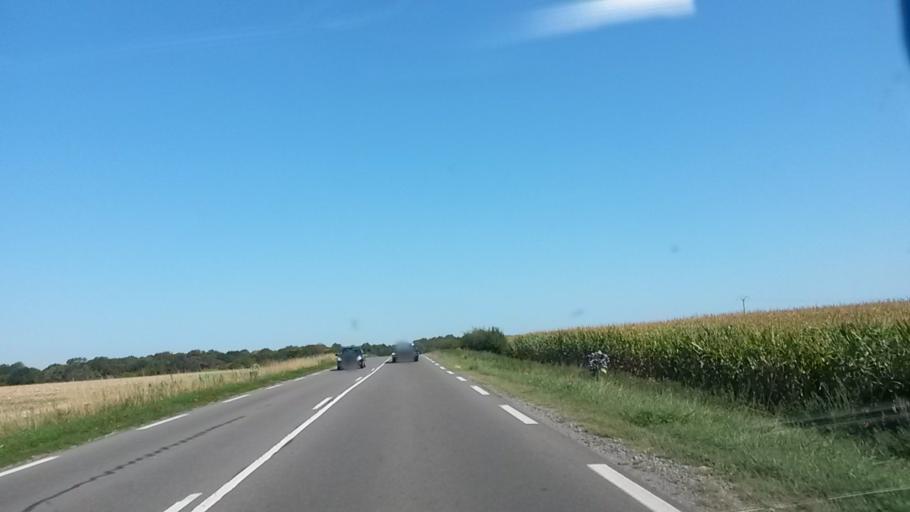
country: FR
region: Nord-Pas-de-Calais
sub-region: Departement du Nord
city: Avesnelles
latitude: 50.1868
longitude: 3.9518
